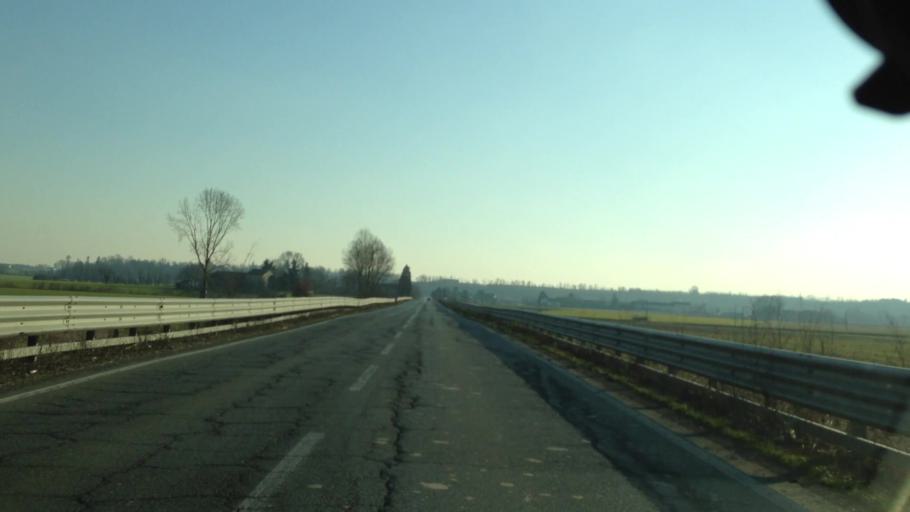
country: IT
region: Piedmont
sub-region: Provincia di Alessandria
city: Felizzano
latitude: 44.8859
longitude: 8.4412
